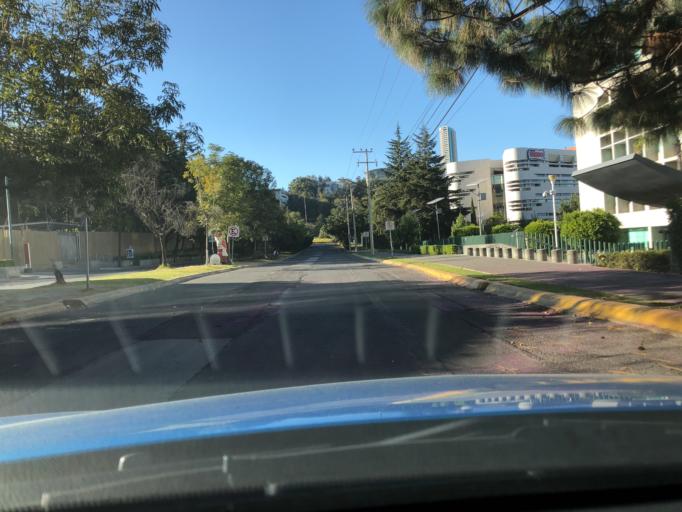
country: MX
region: Mexico City
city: Col. Bosques de las Lomas
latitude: 19.3716
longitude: -99.2613
